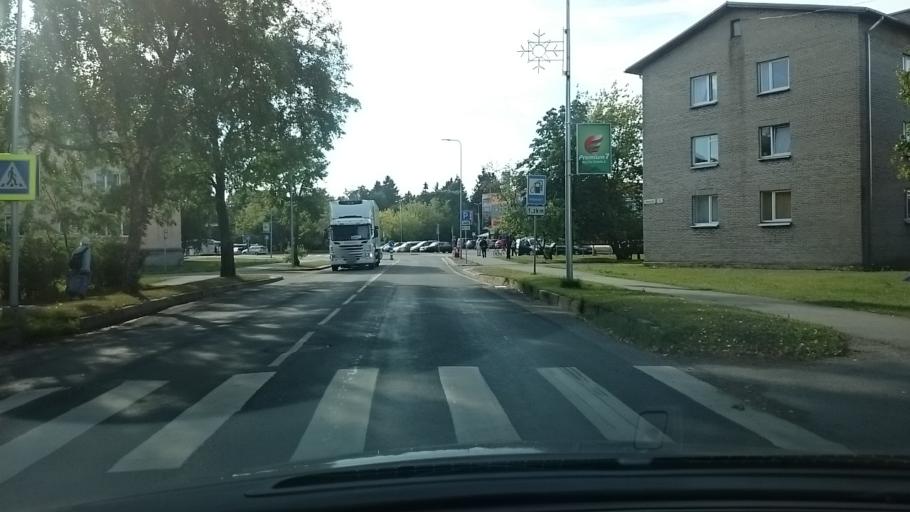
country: EE
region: Laeaene
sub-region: Haapsalu linn
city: Haapsalu
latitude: 58.9394
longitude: 23.5442
